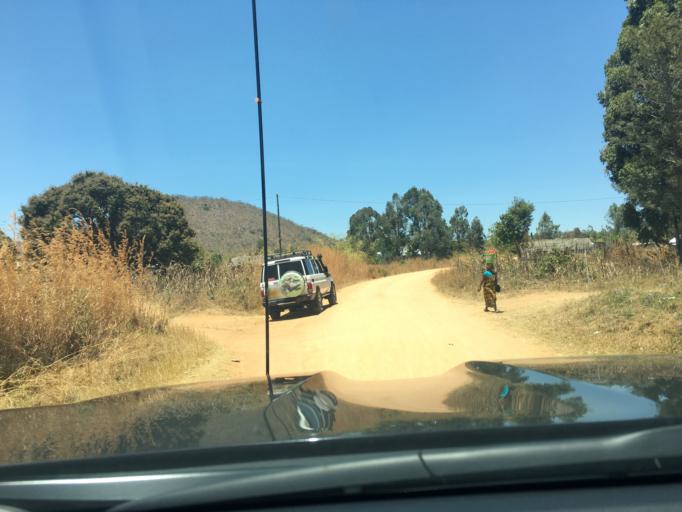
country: TZ
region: Iringa
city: Iringa
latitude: -7.9047
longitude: 35.5902
